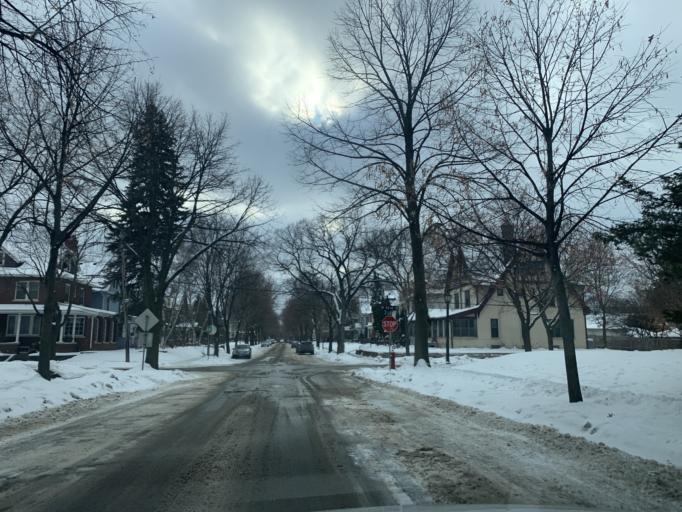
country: US
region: Minnesota
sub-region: Hennepin County
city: Minneapolis
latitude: 44.9613
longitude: -93.2982
